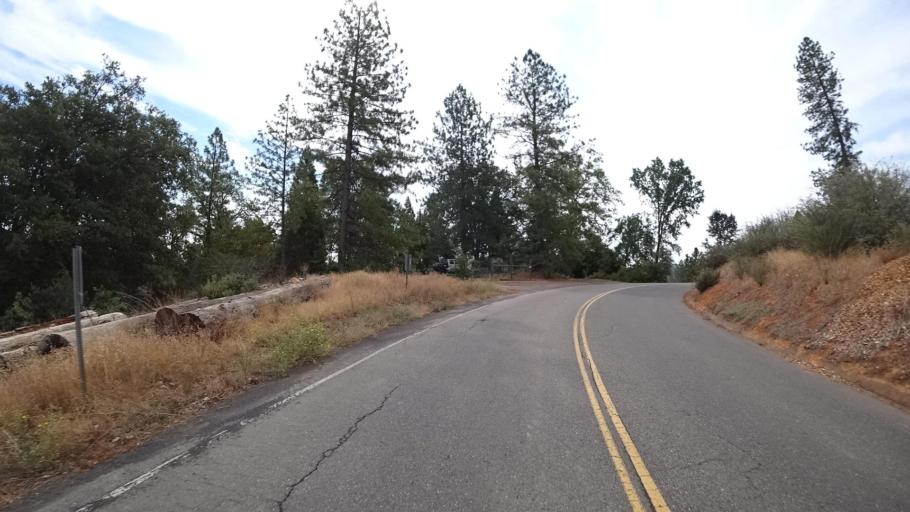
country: US
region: California
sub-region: Mariposa County
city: Midpines
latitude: 37.5257
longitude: -119.9397
